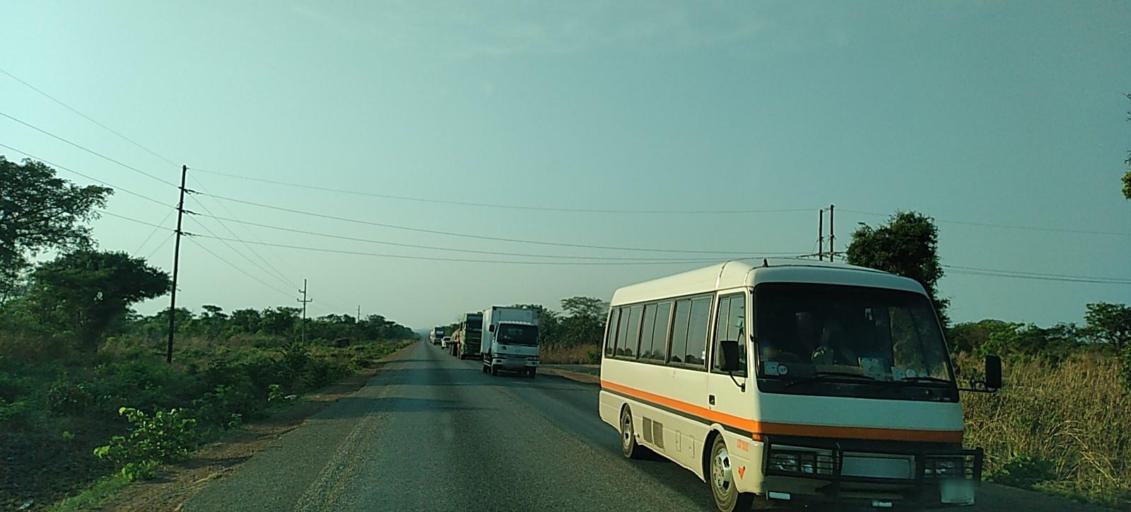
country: ZM
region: Copperbelt
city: Luanshya
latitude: -13.2648
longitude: 28.6784
